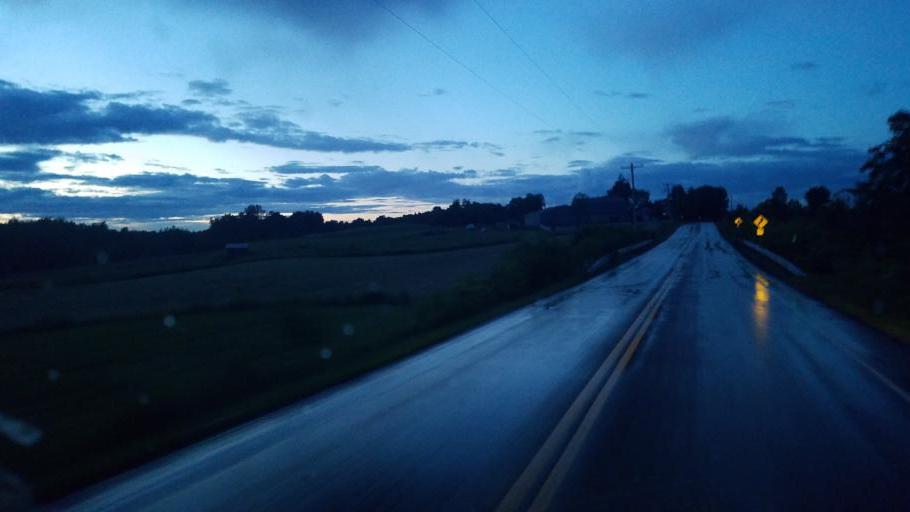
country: US
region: New York
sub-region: Wayne County
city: Clyde
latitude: 43.0408
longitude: -76.9041
